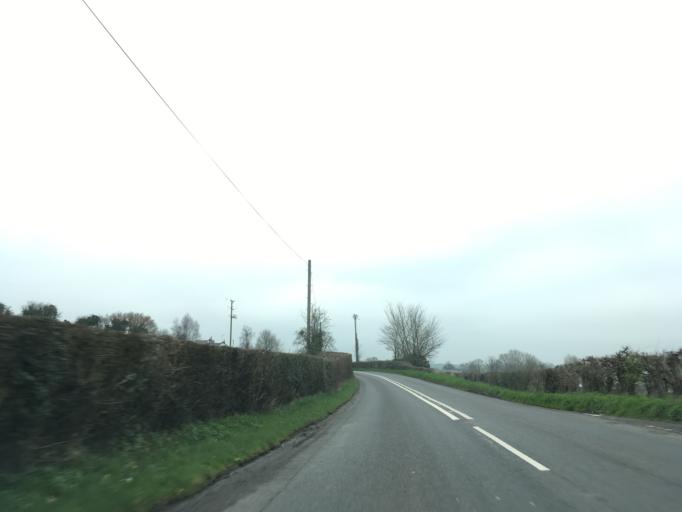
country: GB
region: Wales
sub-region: Monmouthshire
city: Llangybi
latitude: 51.6785
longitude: -2.9064
